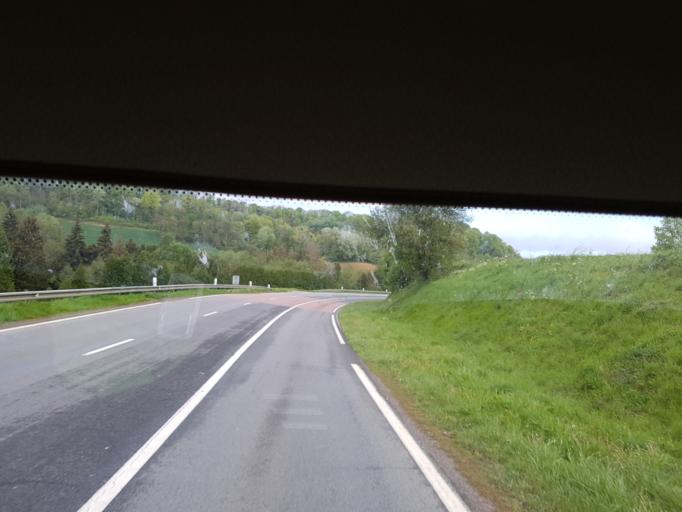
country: FR
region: Picardie
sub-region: Departement de l'Aisne
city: Coucy-le-Chateau-Auffrique
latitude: 49.4818
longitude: 3.3417
